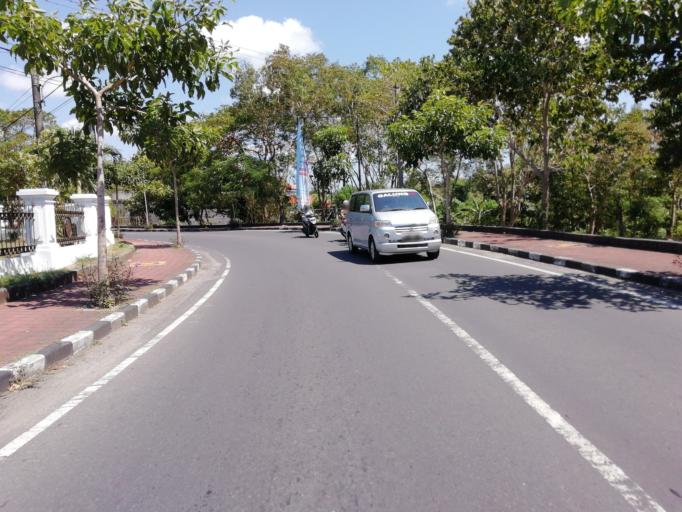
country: ID
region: Bali
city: Jimbaran
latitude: -8.7975
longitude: 115.1732
